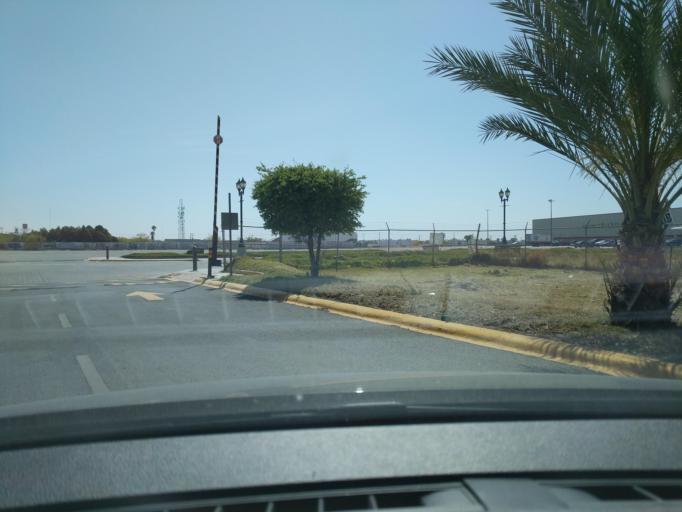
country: MX
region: Coahuila
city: Torreon
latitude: 25.5345
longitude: -103.4041
